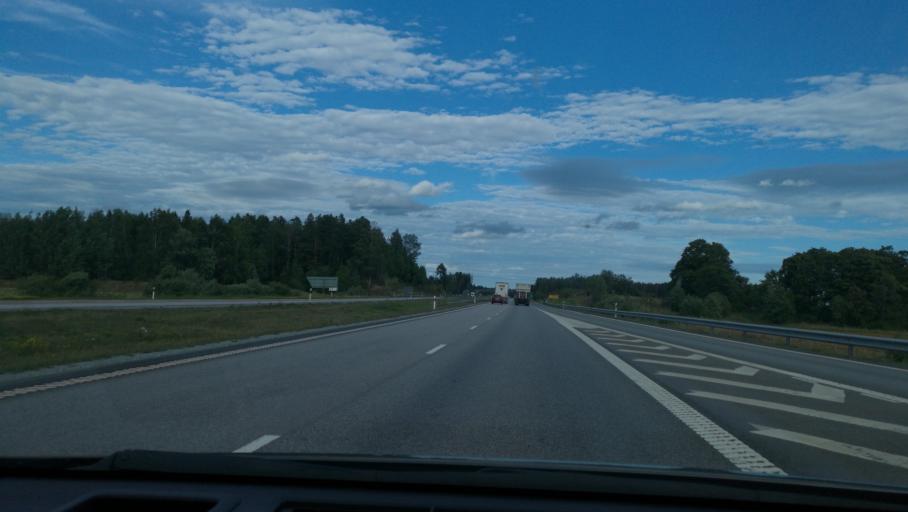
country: SE
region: OErebro
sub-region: Lindesbergs Kommun
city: Frovi
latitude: 59.3100
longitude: 15.4179
